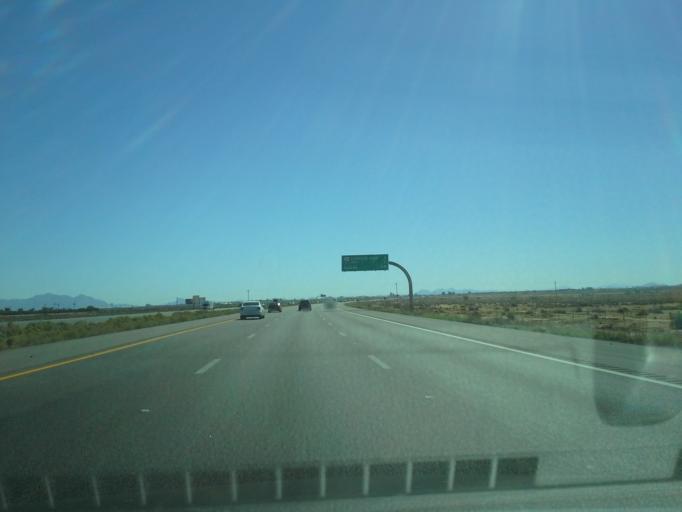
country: US
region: Arizona
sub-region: Pinal County
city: Casa Grande
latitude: 32.9271
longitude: -111.6922
